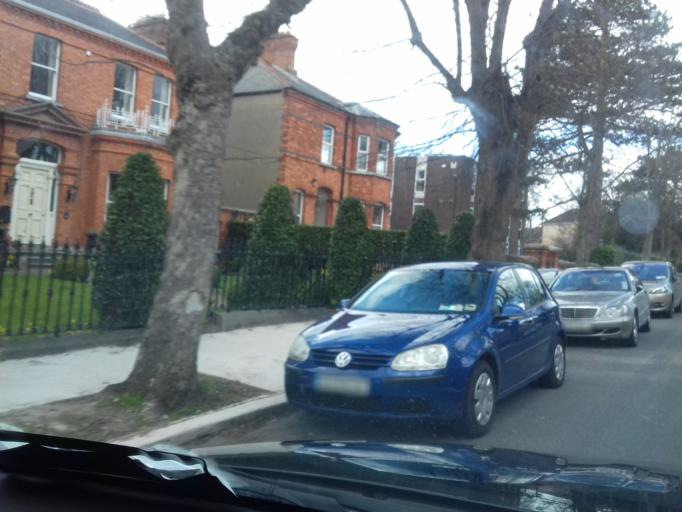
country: IE
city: Donnycarney
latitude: 53.3669
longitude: -6.2135
